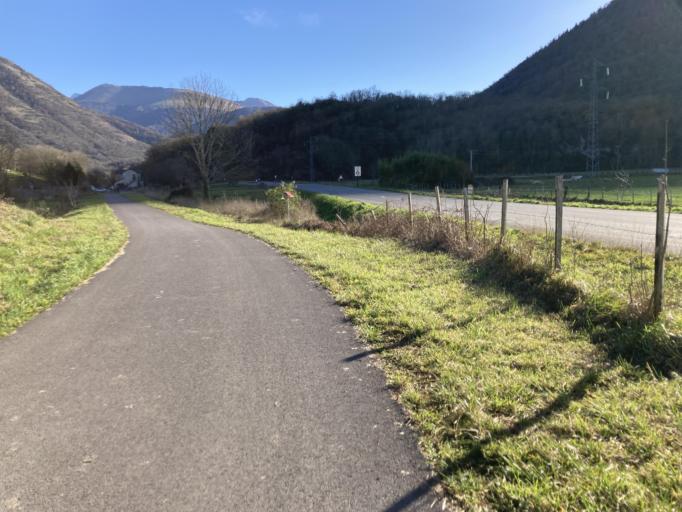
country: FR
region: Aquitaine
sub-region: Departement des Pyrenees-Atlantiques
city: Louvie-Juzon
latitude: 43.0919
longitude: -0.4311
